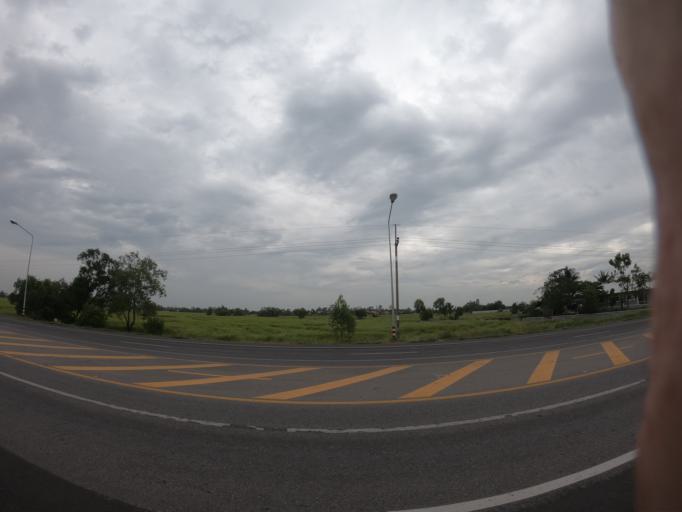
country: TH
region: Roi Et
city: Chiang Khwan
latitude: 16.0986
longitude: 103.7966
